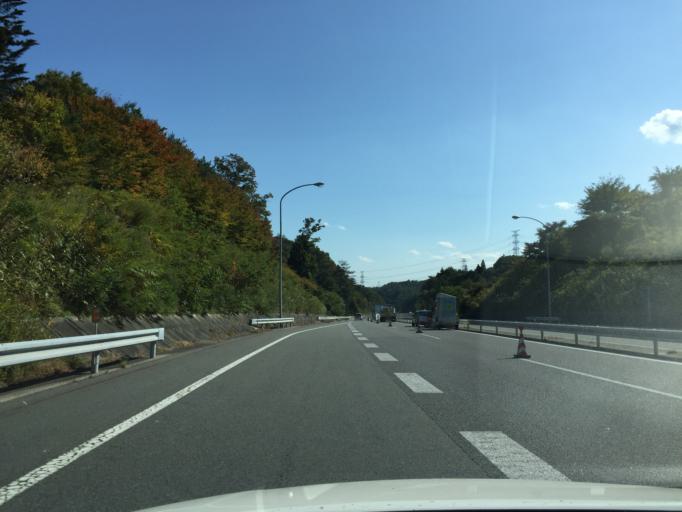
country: JP
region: Fukushima
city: Iwaki
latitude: 37.1741
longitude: 140.7223
